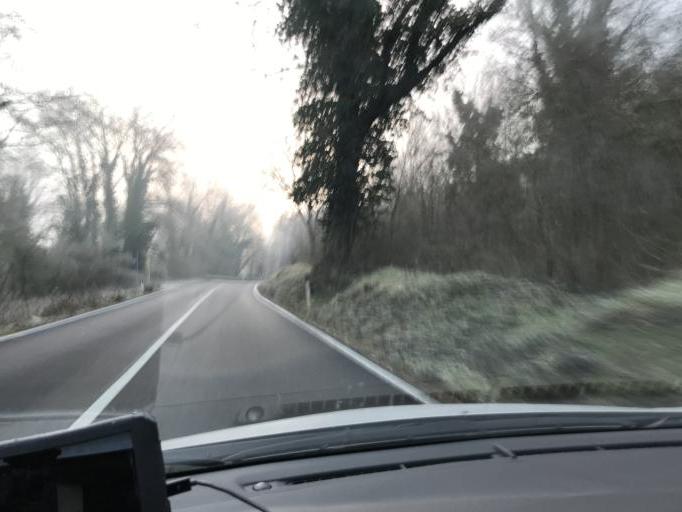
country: IT
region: Latium
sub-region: Provincia di Rieti
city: Colli sul Velino
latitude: 42.5233
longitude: 12.7341
